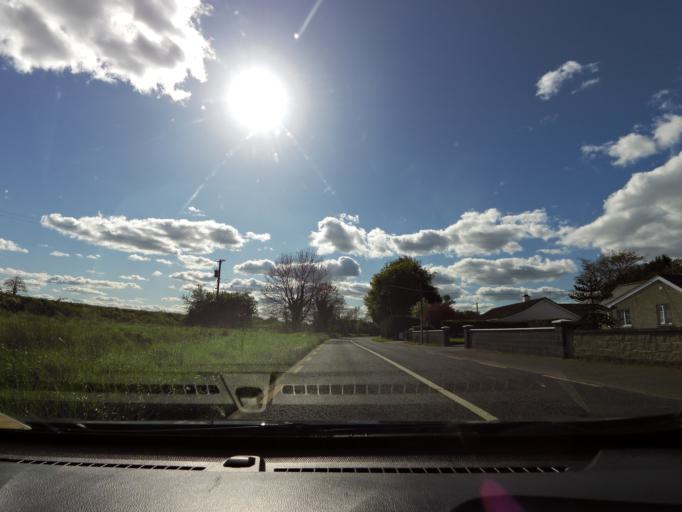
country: IE
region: Leinster
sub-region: Kildare
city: Maynooth
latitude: 53.3834
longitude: -6.6241
